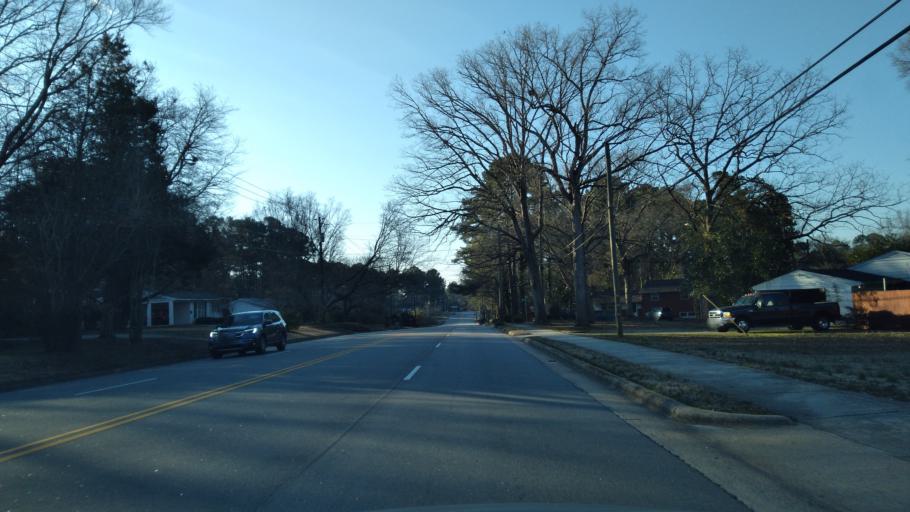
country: US
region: North Carolina
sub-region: Wake County
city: Garner
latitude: 35.7005
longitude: -78.6177
